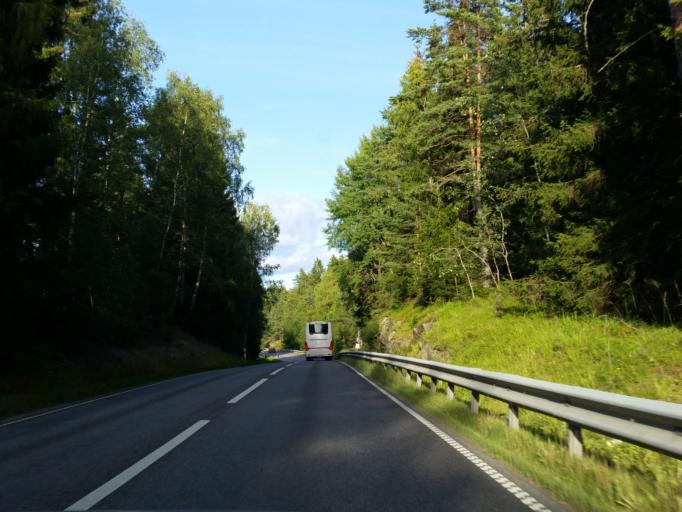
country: SE
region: Stockholm
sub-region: Sodertalje Kommun
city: Molnbo
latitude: 59.0532
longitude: 17.4457
